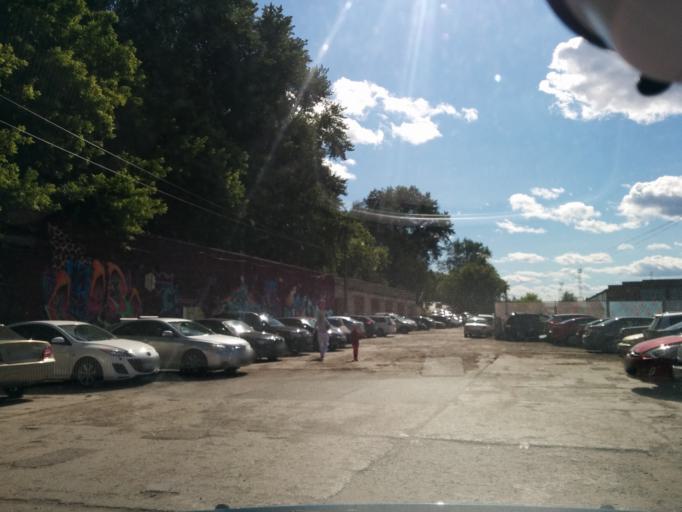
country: RU
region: Perm
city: Perm
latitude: 58.0149
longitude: 56.2108
